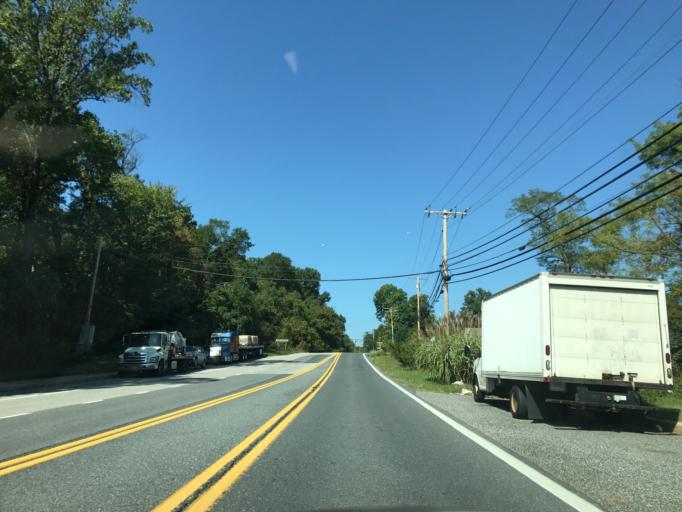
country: US
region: Maryland
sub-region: Anne Arundel County
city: Jessup
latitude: 39.1923
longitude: -76.7739
